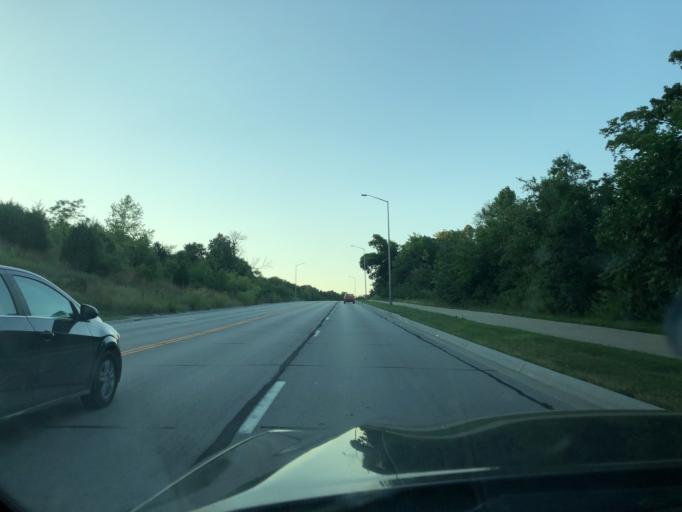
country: US
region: Kansas
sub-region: Leavenworth County
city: Leavenworth
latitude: 39.2967
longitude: -94.9515
